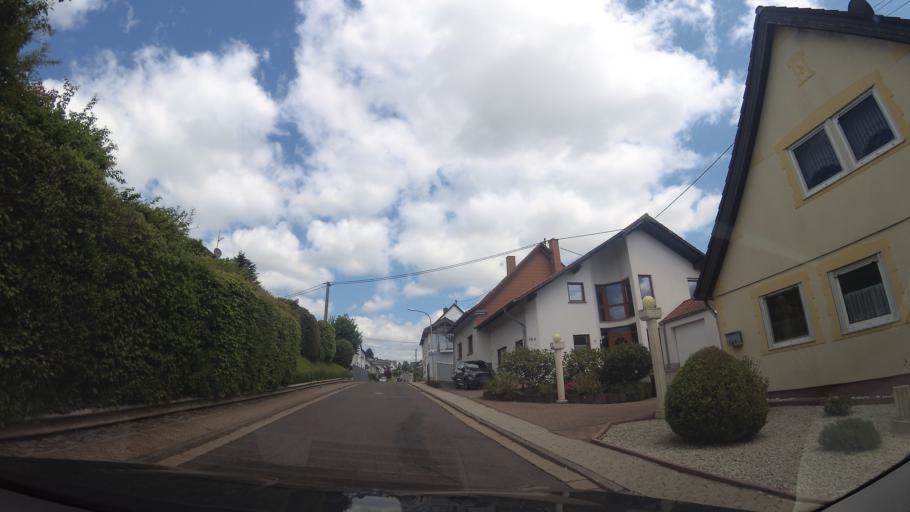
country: DE
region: Saarland
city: Lebach
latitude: 49.4159
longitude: 6.9151
